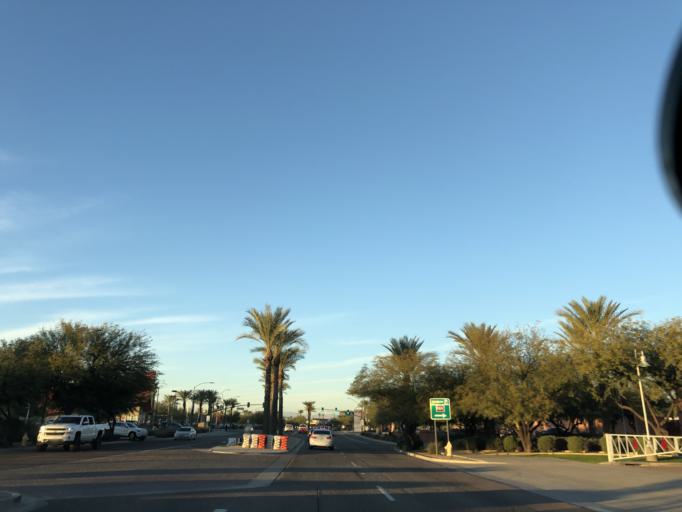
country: US
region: Arizona
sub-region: Maricopa County
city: Peoria
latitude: 33.5315
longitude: -112.2647
